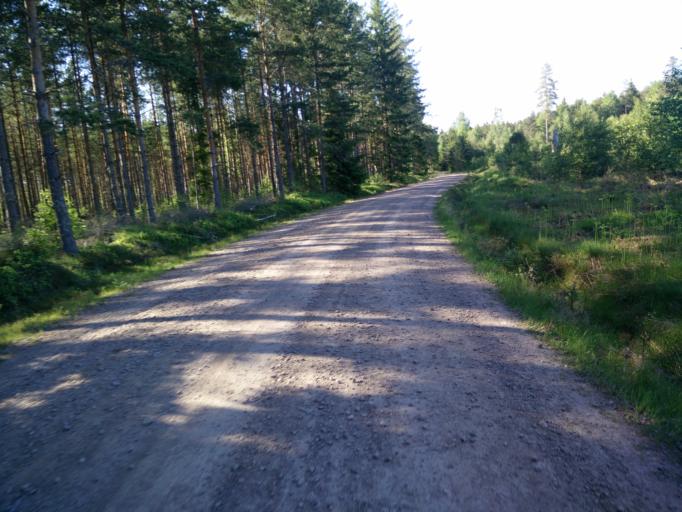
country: SE
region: Vaermland
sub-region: Hagfors Kommun
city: Hagfors
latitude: 60.0227
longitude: 13.5556
